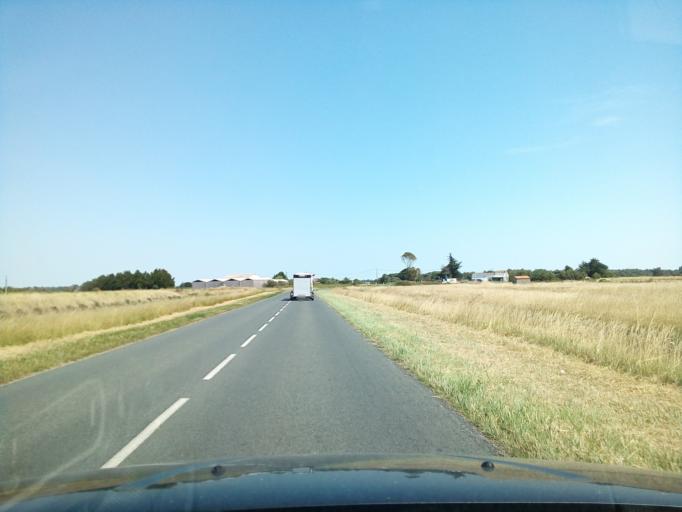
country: FR
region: Poitou-Charentes
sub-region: Departement de la Charente-Maritime
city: Boyard-Ville
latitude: 45.9681
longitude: -1.2716
